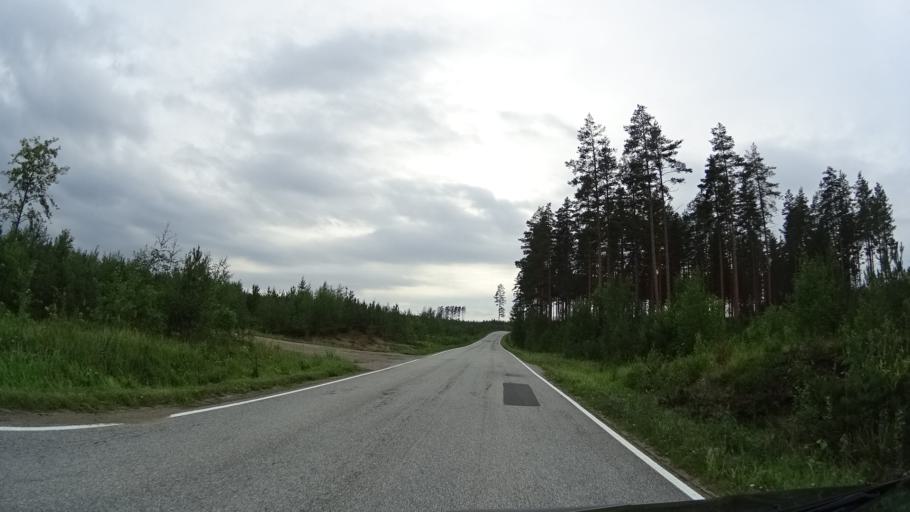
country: FI
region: Southern Savonia
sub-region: Savonlinna
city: Punkaharju
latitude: 61.7497
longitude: 29.4779
